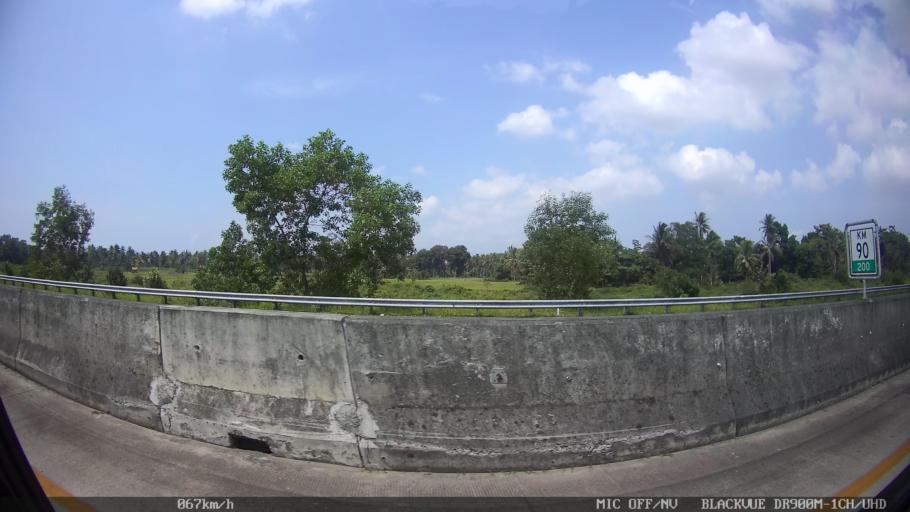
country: ID
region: Lampung
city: Natar
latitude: -5.3060
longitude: 105.2467
